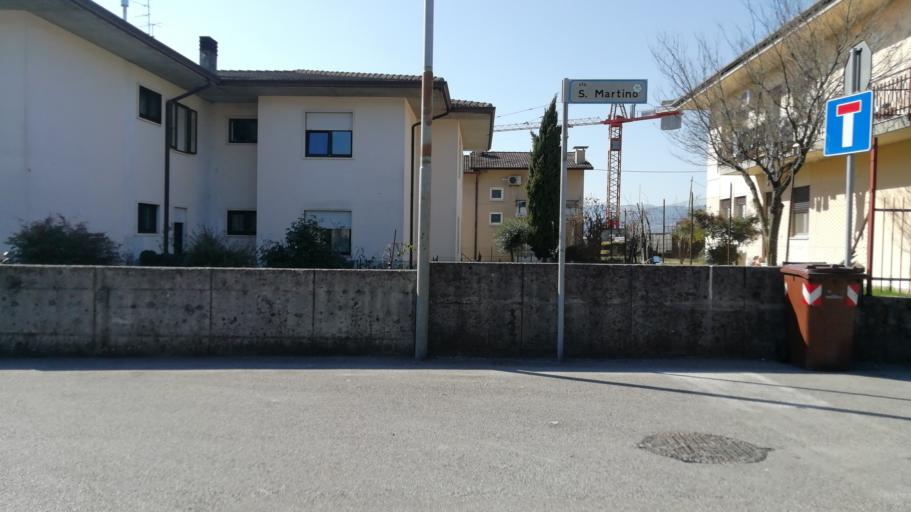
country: IT
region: Veneto
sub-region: Provincia di Vicenza
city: Thiene
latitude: 45.7017
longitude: 11.4631
